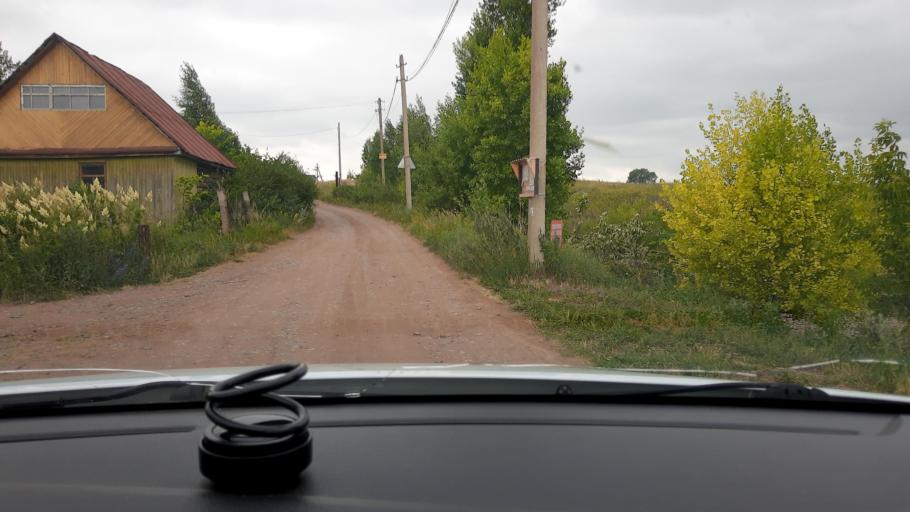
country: RU
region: Bashkortostan
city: Avdon
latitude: 54.6392
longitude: 55.5718
